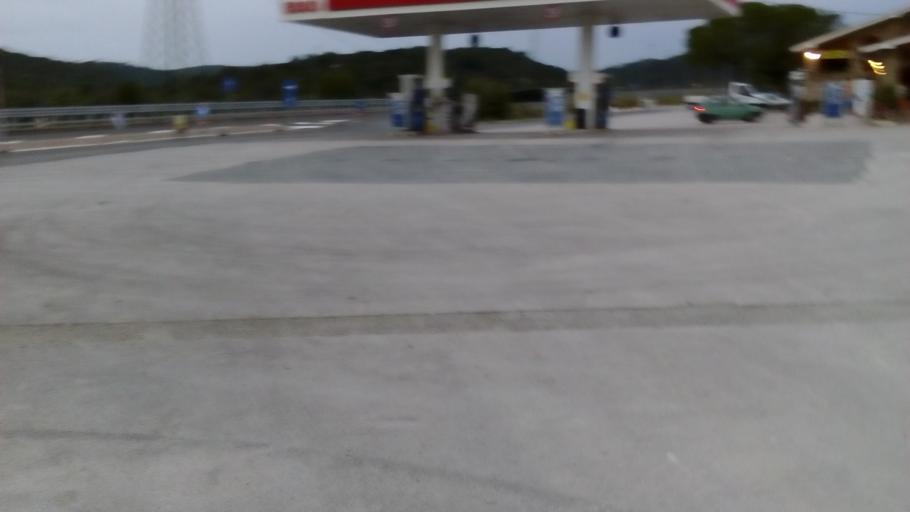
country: IT
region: Tuscany
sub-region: Provincia di Grosseto
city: Civitella Marittima
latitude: 43.0283
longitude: 11.2789
